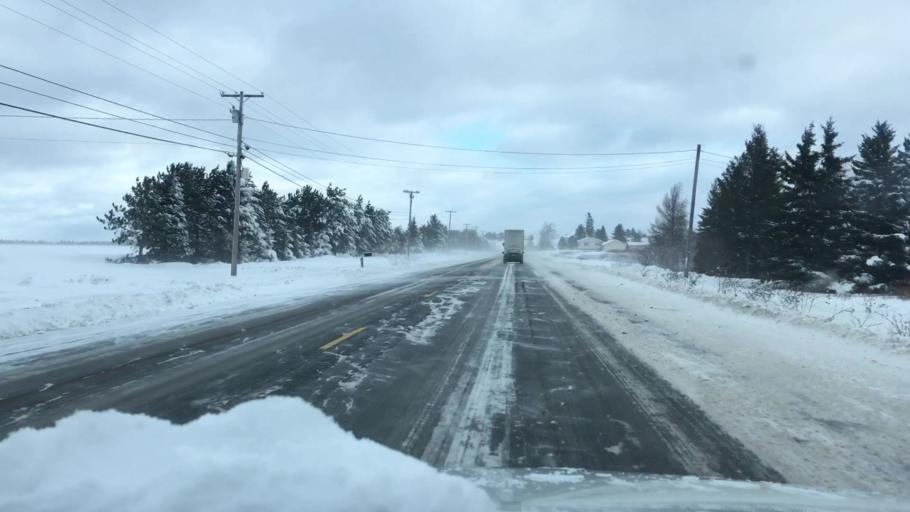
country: US
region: Maine
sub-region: Aroostook County
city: Presque Isle
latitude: 46.7383
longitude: -67.9983
